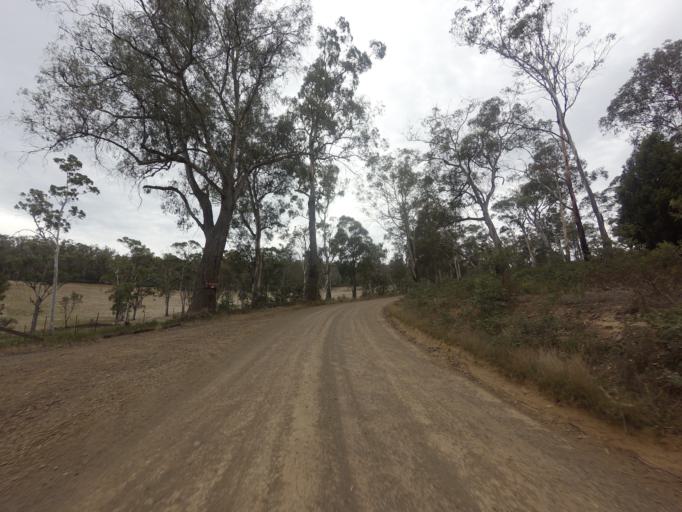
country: AU
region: Tasmania
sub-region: Derwent Valley
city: New Norfolk
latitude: -42.5622
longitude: 146.9415
